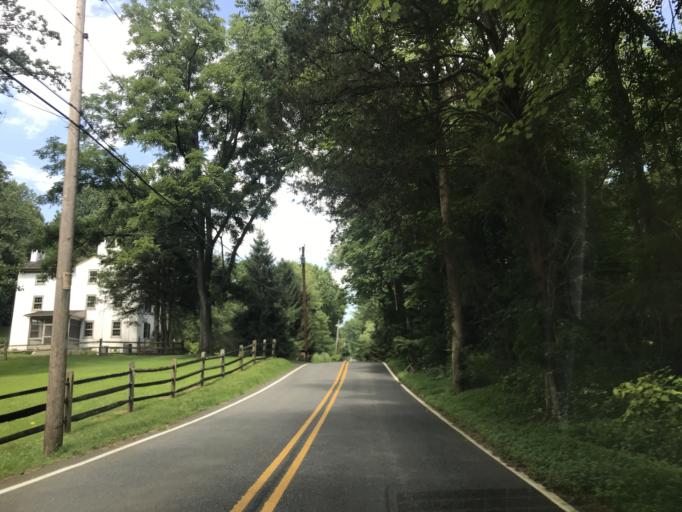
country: US
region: Delaware
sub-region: New Castle County
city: Greenville
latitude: 39.8476
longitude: -75.5637
